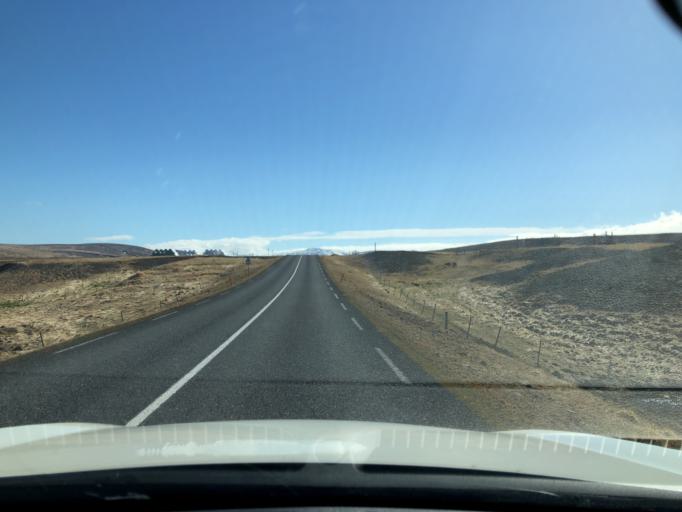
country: IS
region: South
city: Hveragerdi
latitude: 64.7015
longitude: -21.2001
